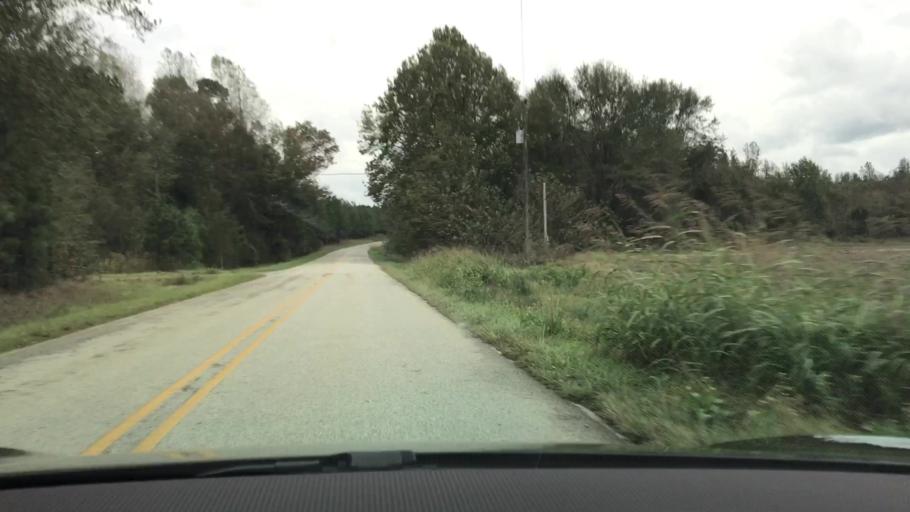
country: US
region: Georgia
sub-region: Jefferson County
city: Wadley
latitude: 32.8394
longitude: -82.3924
